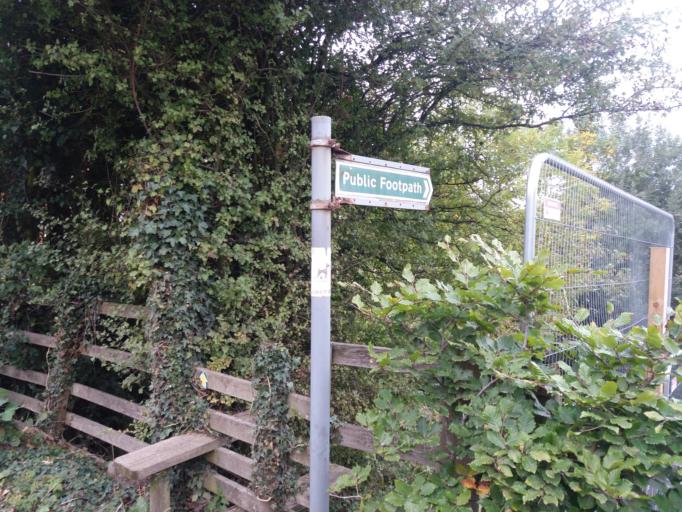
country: GB
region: England
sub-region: Lancashire
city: Chorley
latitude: 53.6766
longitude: -2.6320
